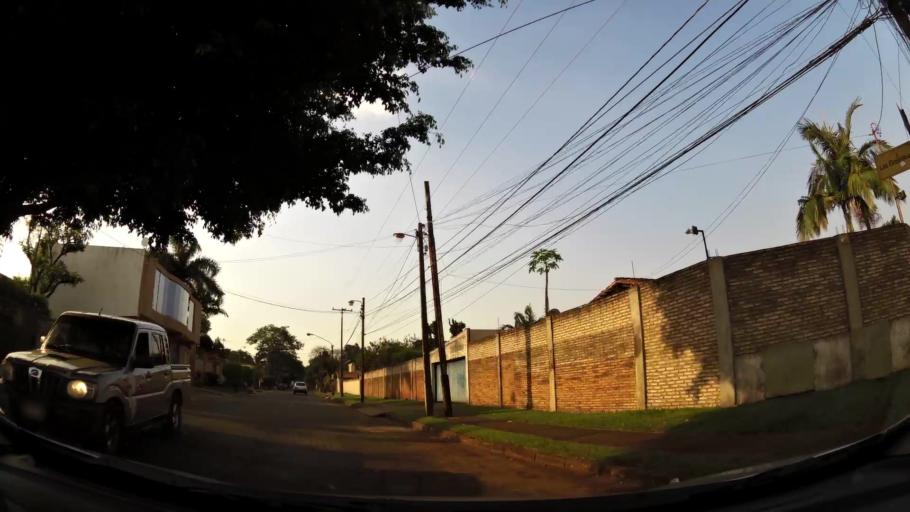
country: PY
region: Alto Parana
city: Presidente Franco
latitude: -25.5217
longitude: -54.6383
